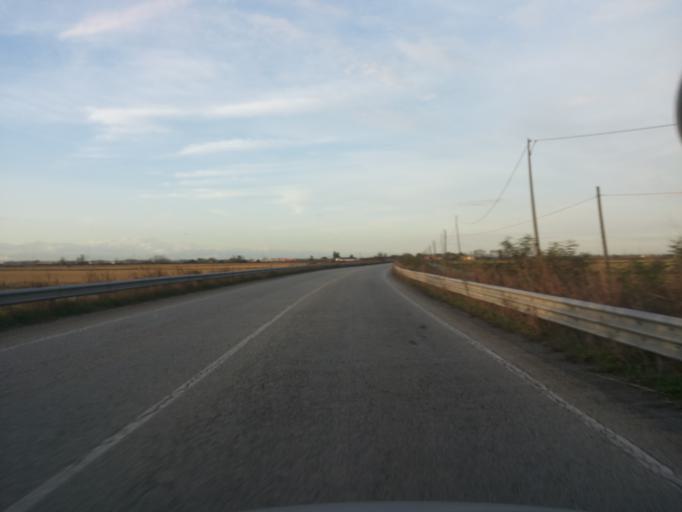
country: IT
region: Piedmont
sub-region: Provincia di Alessandria
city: Pontestura
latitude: 45.1587
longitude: 8.3319
